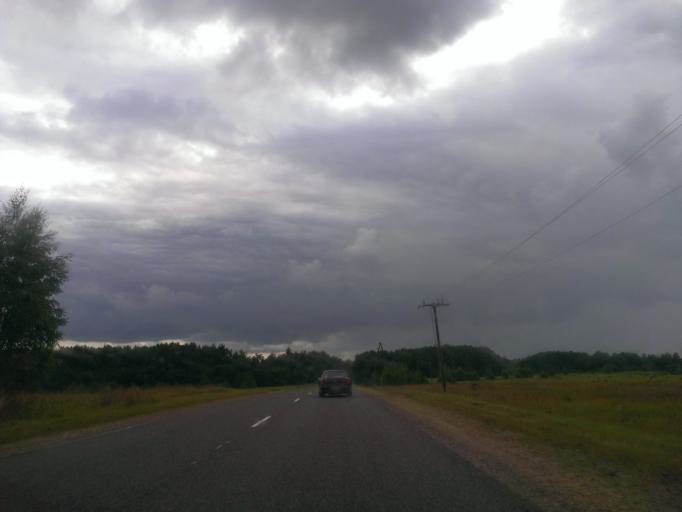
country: LV
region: Kegums
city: Kegums
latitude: 56.7608
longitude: 24.7491
